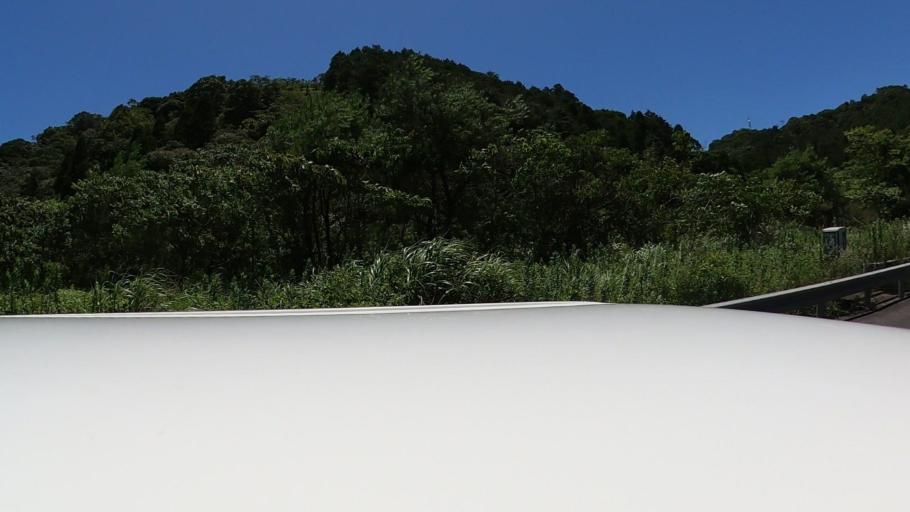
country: JP
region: Miyazaki
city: Nobeoka
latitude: 32.5394
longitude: 131.6577
